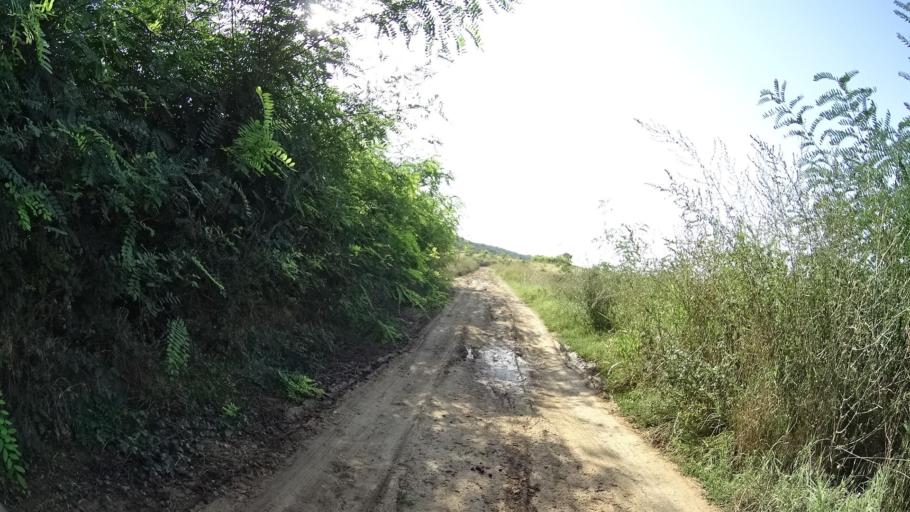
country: BG
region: Plovdiv
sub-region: Obshtina Plovdiv
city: Plovdiv
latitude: 42.0639
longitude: 24.6972
